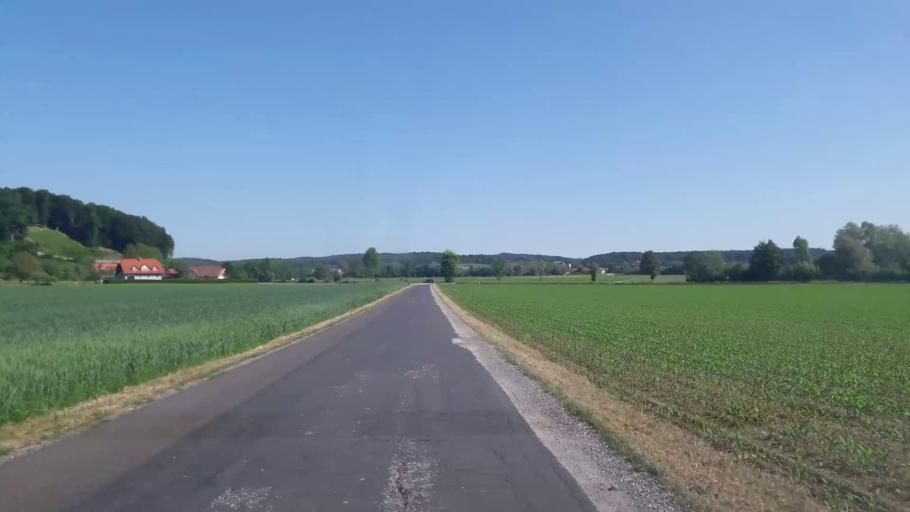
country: AT
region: Styria
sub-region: Politischer Bezirk Hartberg-Fuerstenfeld
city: UEbersbach
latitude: 47.0102
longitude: 16.0506
